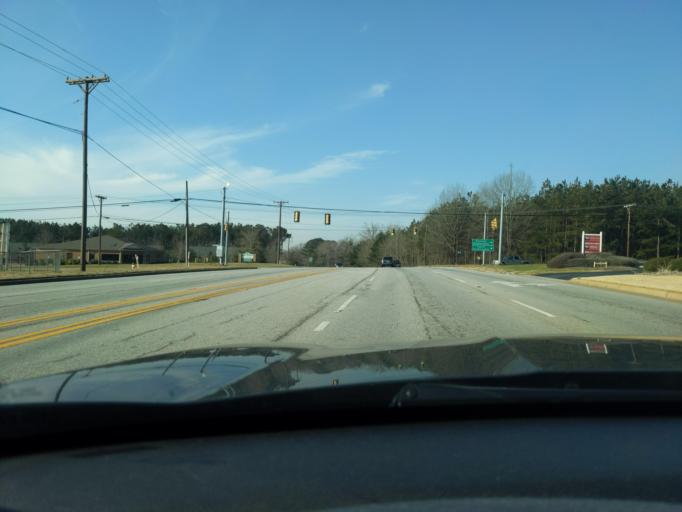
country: US
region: South Carolina
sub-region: Greenwood County
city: Greenwood
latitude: 34.2021
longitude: -82.2009
